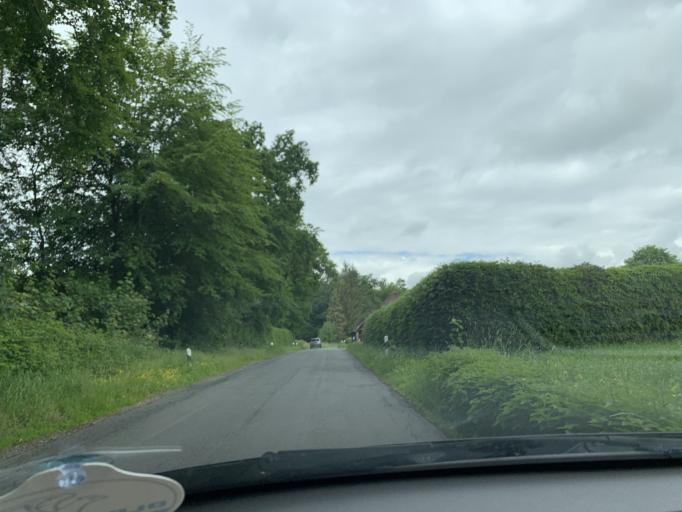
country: DE
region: Lower Saxony
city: Varel
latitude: 53.3814
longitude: 8.0767
